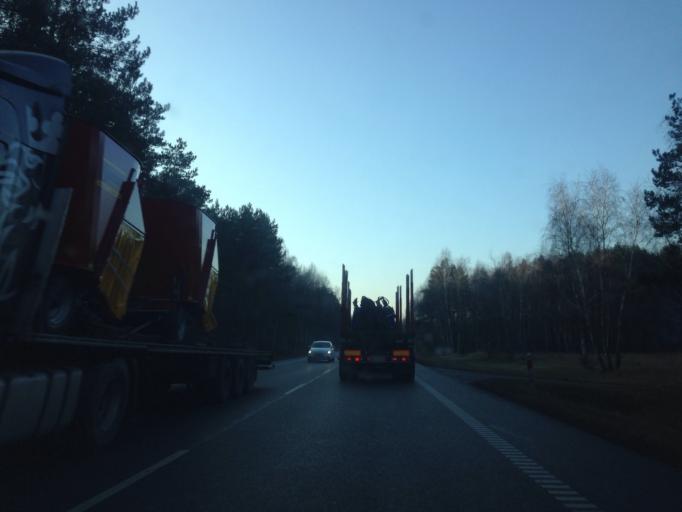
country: PL
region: Kujawsko-Pomorskie
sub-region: Powiat bydgoski
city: Solec Kujawski
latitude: 53.0588
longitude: 18.2787
